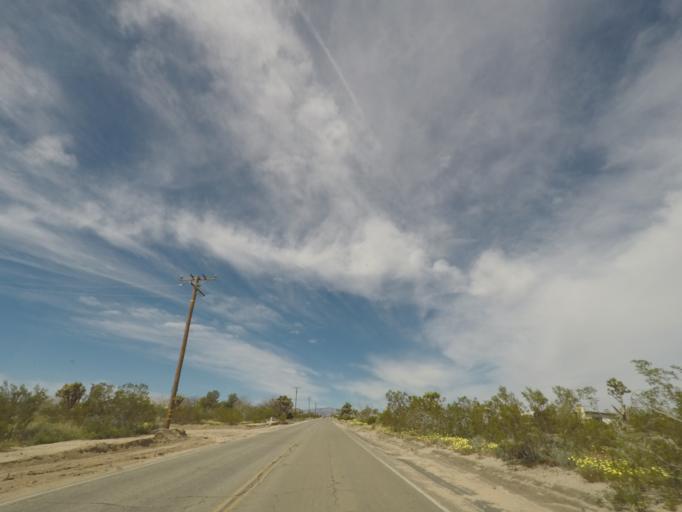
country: US
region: California
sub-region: San Bernardino County
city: Joshua Tree
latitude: 34.1930
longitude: -116.3646
